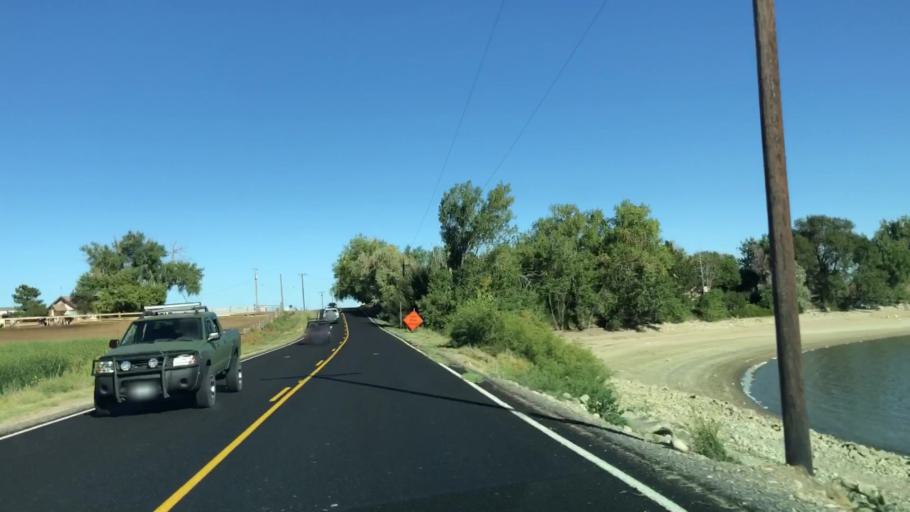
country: US
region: Colorado
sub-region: Larimer County
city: Loveland
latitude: 40.4509
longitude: -105.0512
